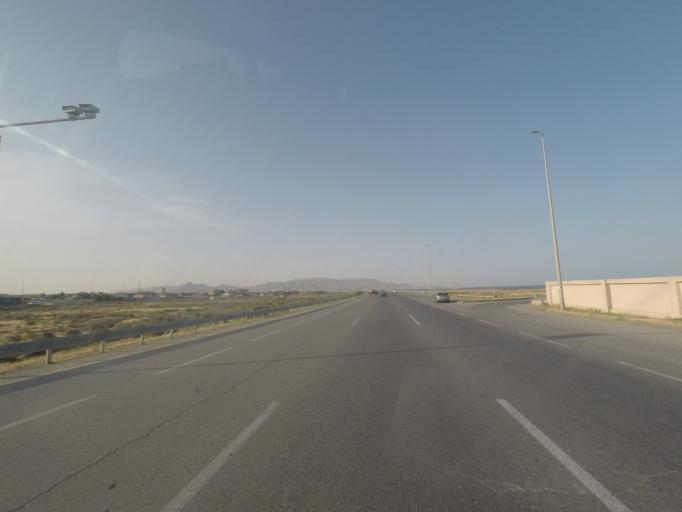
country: AZ
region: Baki
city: Qobustan
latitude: 40.1581
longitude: 49.4617
